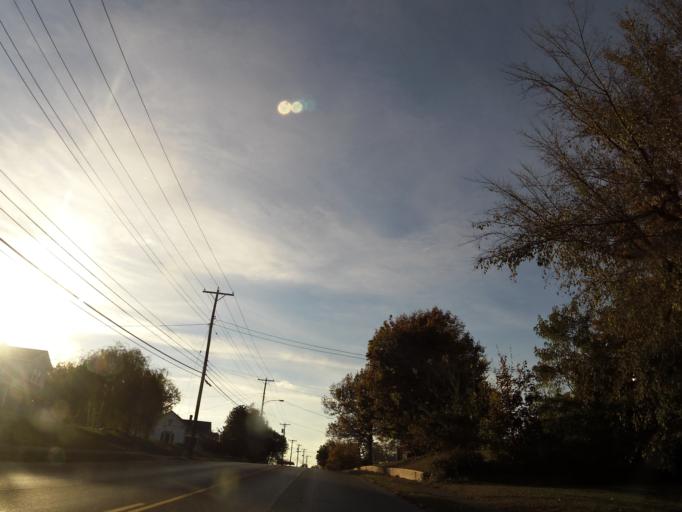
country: US
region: Kentucky
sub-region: Garrard County
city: Lancaster
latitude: 37.6200
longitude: -84.5857
